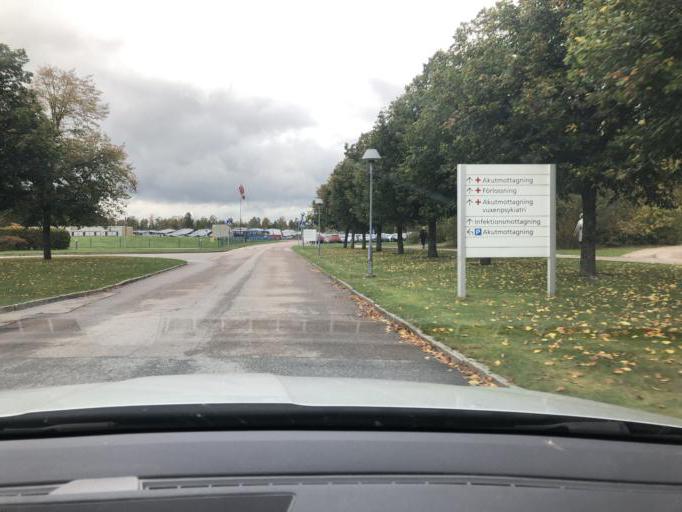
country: SE
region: Vaestra Goetaland
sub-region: Trollhattan
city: Trollhattan
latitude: 58.3180
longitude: 12.2688
